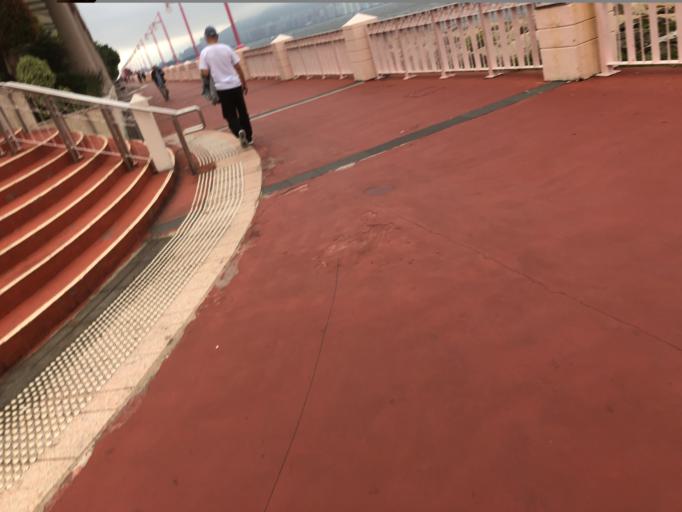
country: HK
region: Tai Po
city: Tai Po
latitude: 22.4526
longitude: 114.1869
